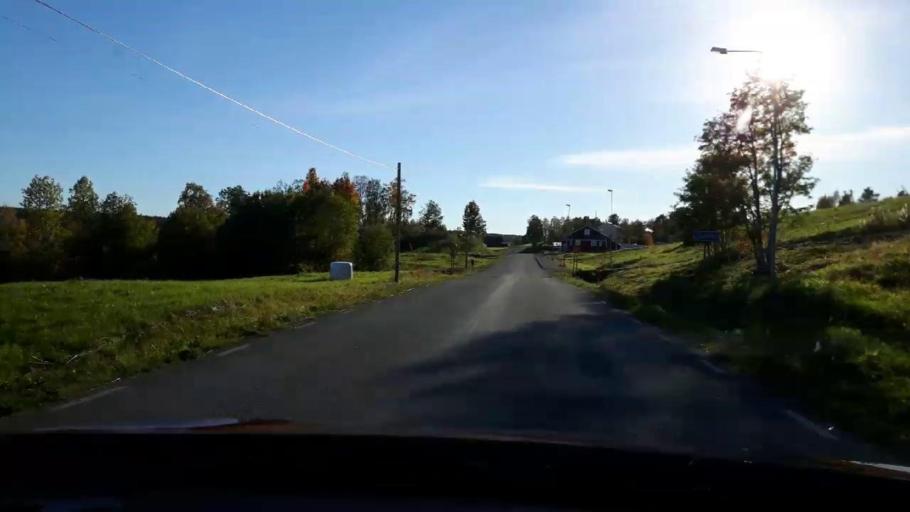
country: SE
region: Jaemtland
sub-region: OEstersunds Kommun
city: Lit
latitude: 63.8164
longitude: 14.8104
